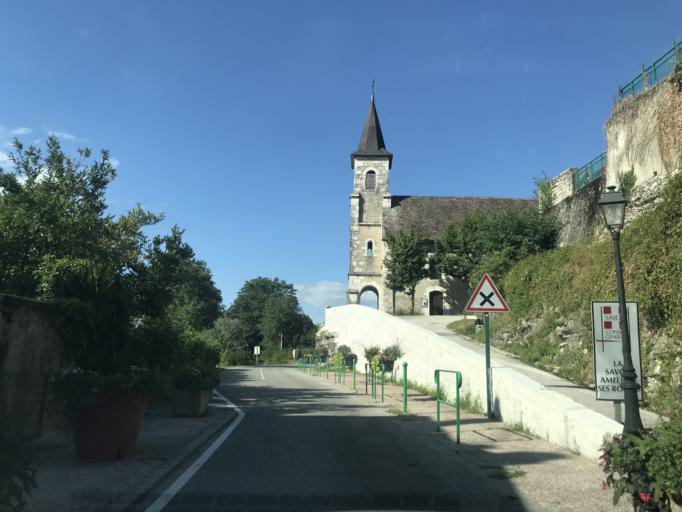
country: FR
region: Rhone-Alpes
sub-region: Departement de l'Ain
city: Culoz
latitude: 45.8096
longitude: 5.7946
